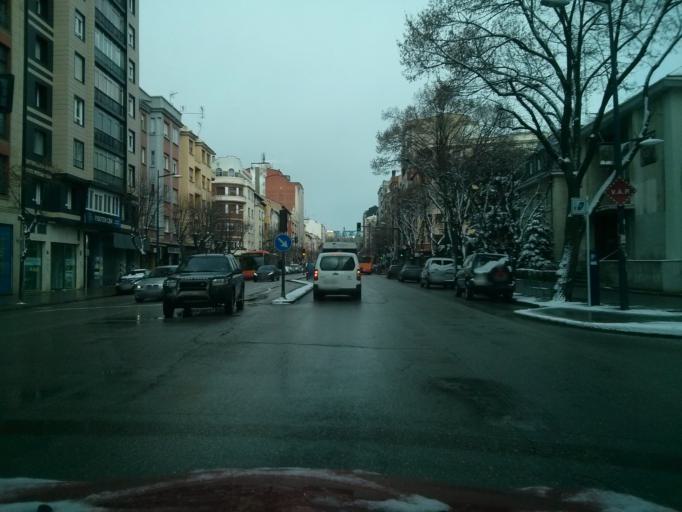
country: ES
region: Castille and Leon
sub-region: Provincia de Burgos
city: Burgos
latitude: 42.3475
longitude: -3.6971
